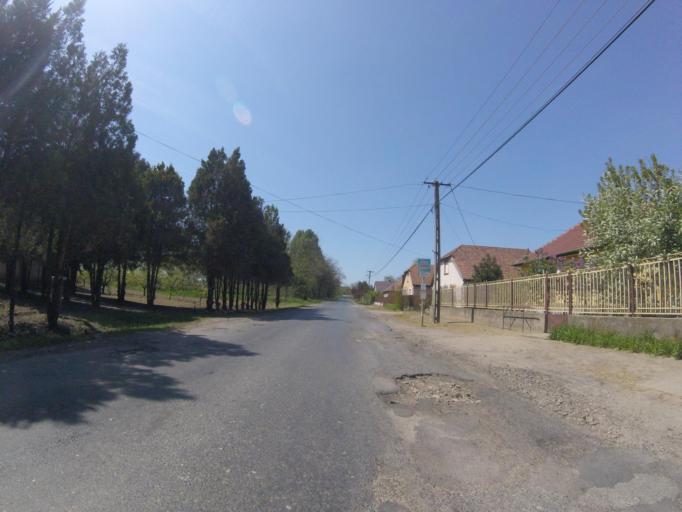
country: HU
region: Pest
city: Danszentmiklos
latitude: 47.2190
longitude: 19.5212
